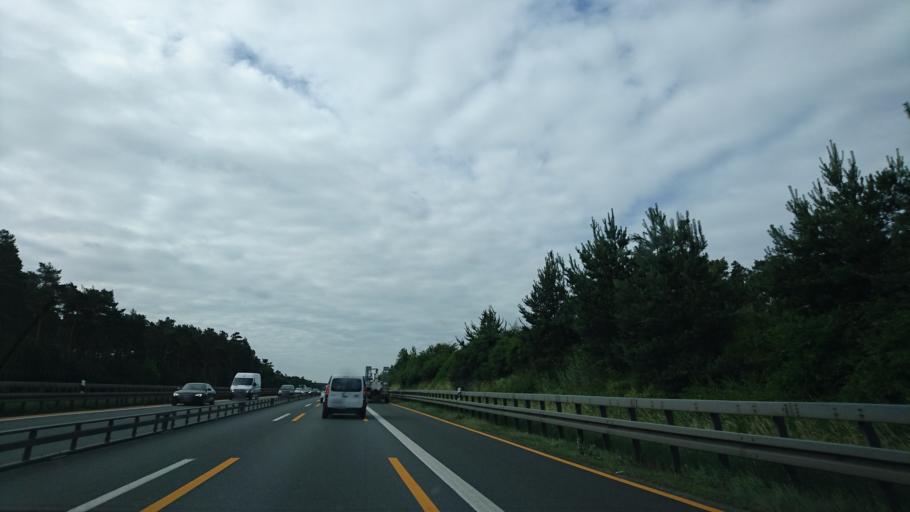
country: DE
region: Bavaria
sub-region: Regierungsbezirk Mittelfranken
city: Allersberg
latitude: 49.3038
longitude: 11.2079
